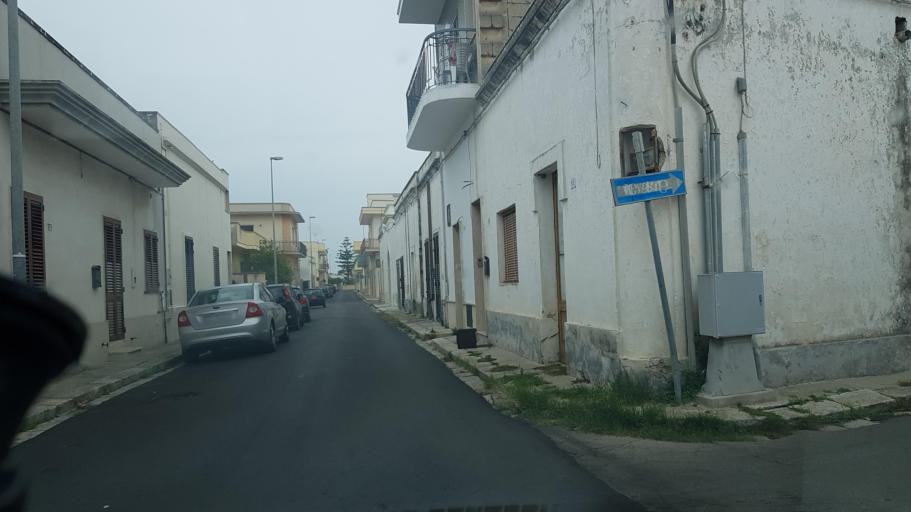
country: IT
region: Apulia
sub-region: Provincia di Lecce
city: Leverano
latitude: 40.2922
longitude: 18.0018
